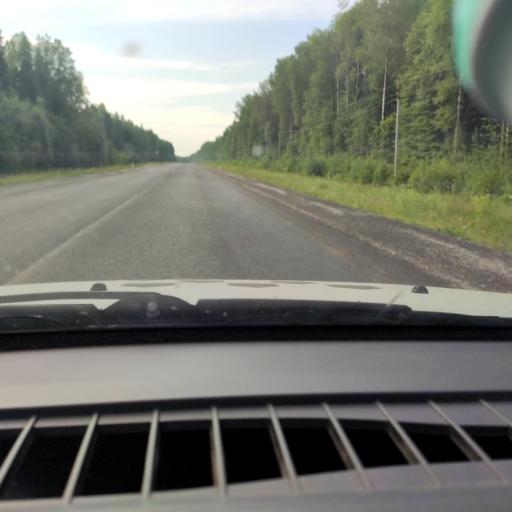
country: RU
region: Perm
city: Siva
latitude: 58.5686
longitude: 53.8889
